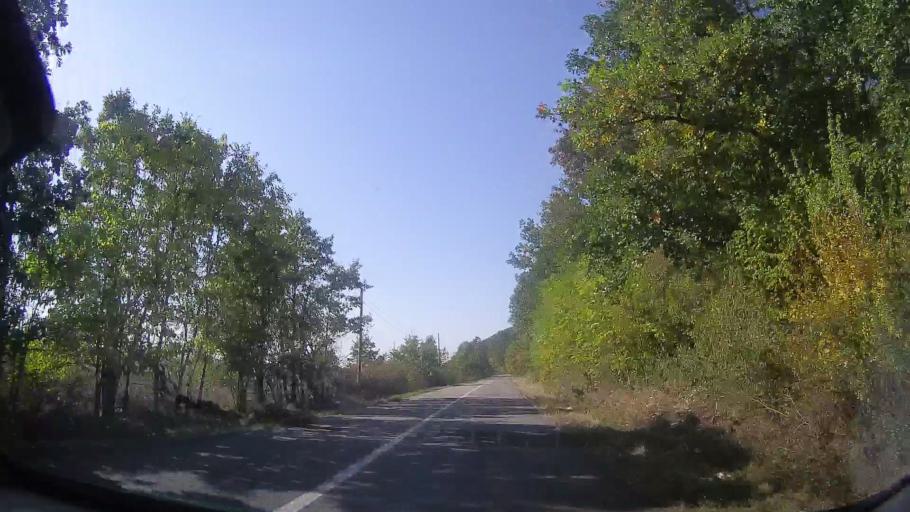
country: RO
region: Timis
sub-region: Comuna Ghizela
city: Ghizela
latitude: 45.8361
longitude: 21.7753
